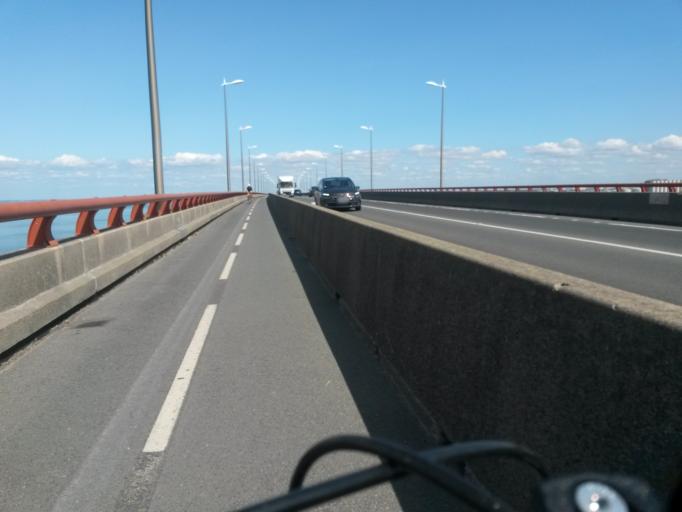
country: FR
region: Poitou-Charentes
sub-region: Departement de la Charente-Maritime
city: Rivedoux-Plage
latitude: 46.1698
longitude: -1.2452
